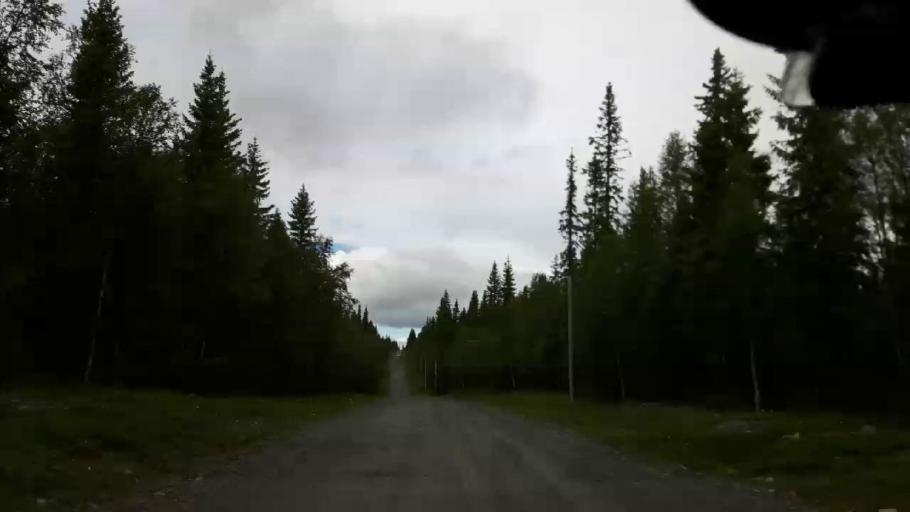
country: SE
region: Jaemtland
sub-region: Krokoms Kommun
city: Valla
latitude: 63.7197
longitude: 13.8567
